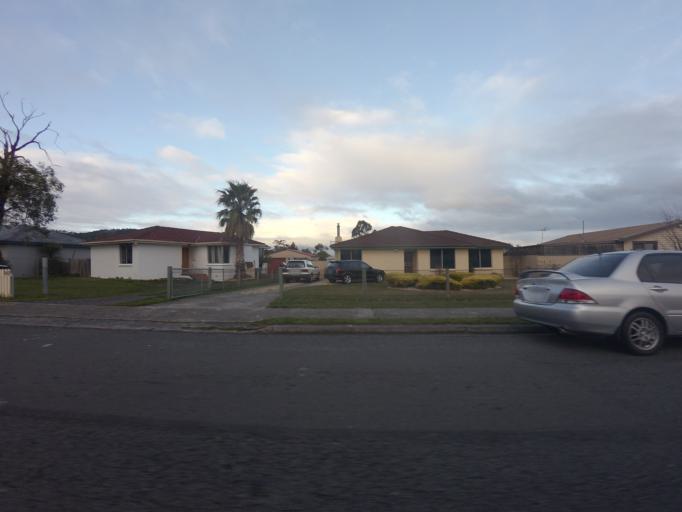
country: AU
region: Tasmania
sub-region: Clarence
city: Rokeby
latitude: -42.9020
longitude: 147.4354
